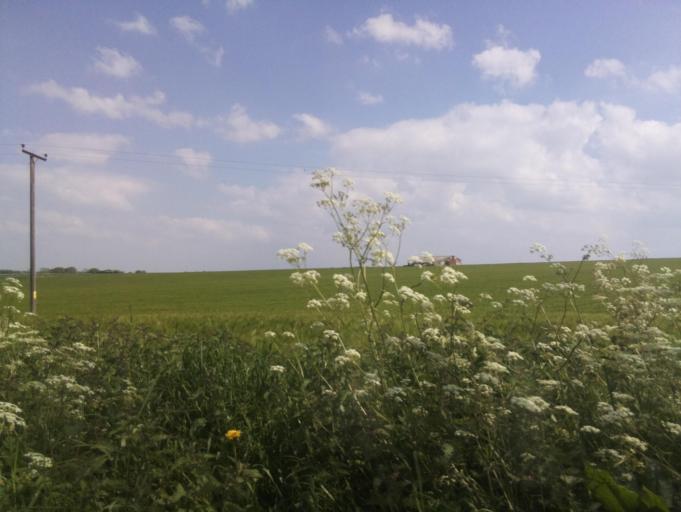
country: GB
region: England
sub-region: South Gloucestershire
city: Horton
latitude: 51.5718
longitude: -2.3240
